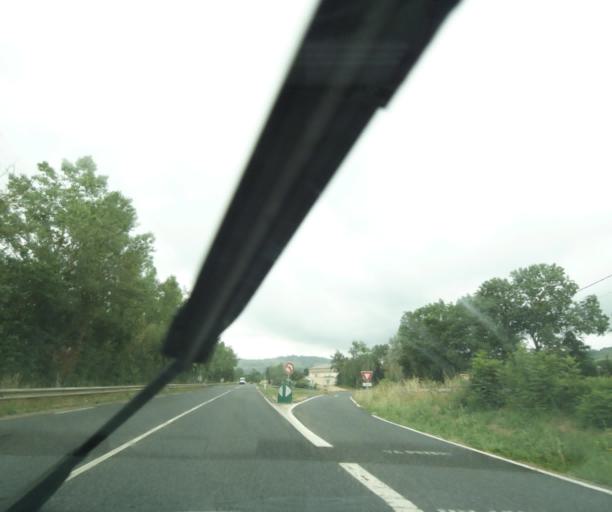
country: FR
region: Midi-Pyrenees
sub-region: Departement de l'Aveyron
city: Severac-le-Chateau
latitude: 44.3384
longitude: 3.0276
